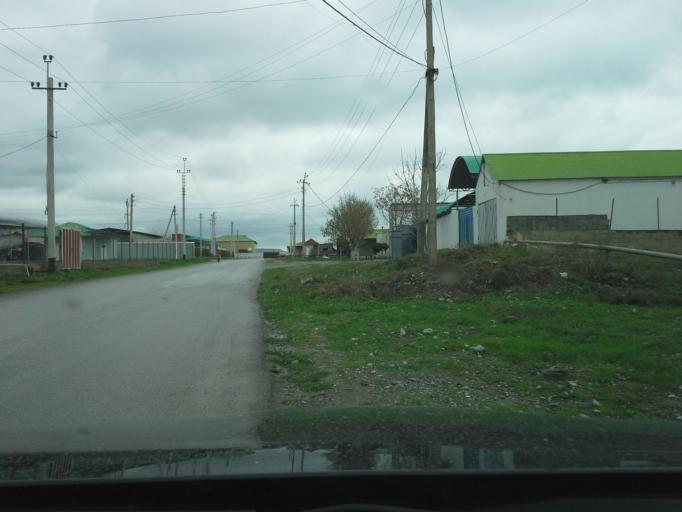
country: TM
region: Ahal
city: Abadan
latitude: 37.9493
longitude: 58.2075
